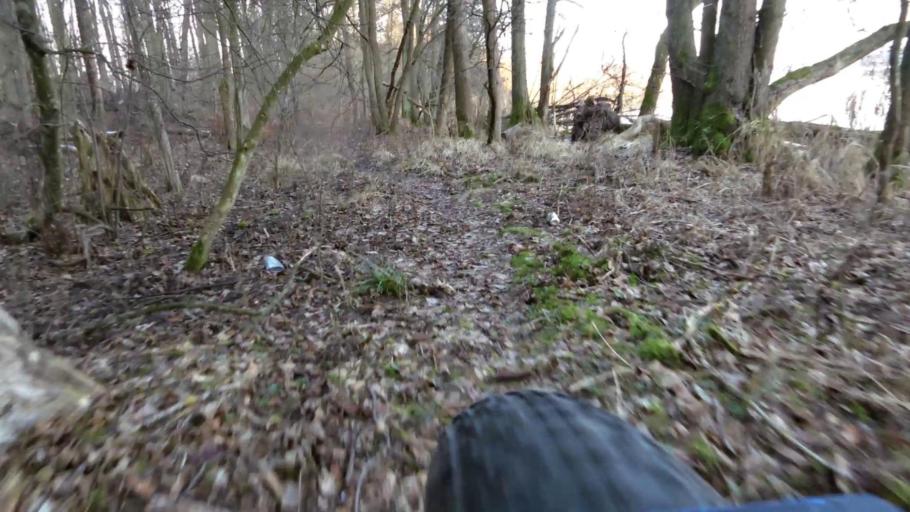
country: PL
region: West Pomeranian Voivodeship
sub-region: Powiat walecki
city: Walcz
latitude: 53.2511
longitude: 16.3791
